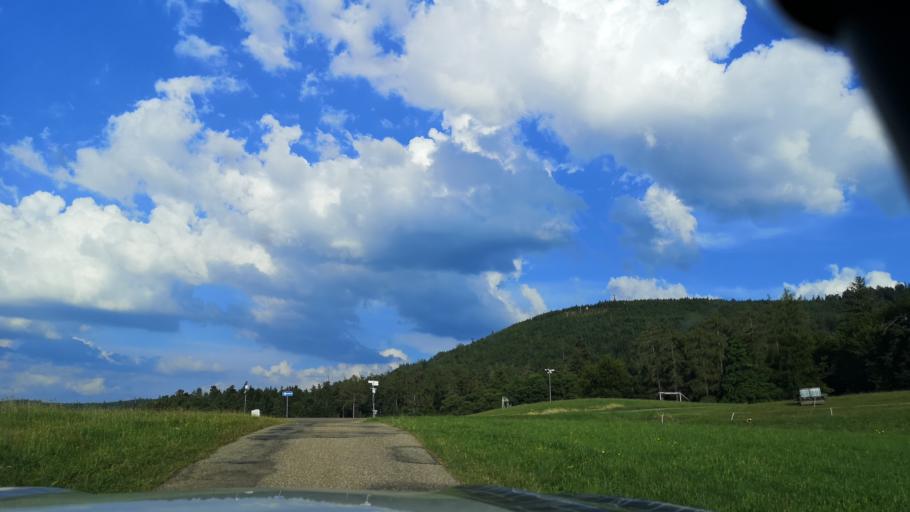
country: DE
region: Baden-Wuerttemberg
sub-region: Karlsruhe Region
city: Bad Herrenalb
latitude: 48.7682
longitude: 8.4401
